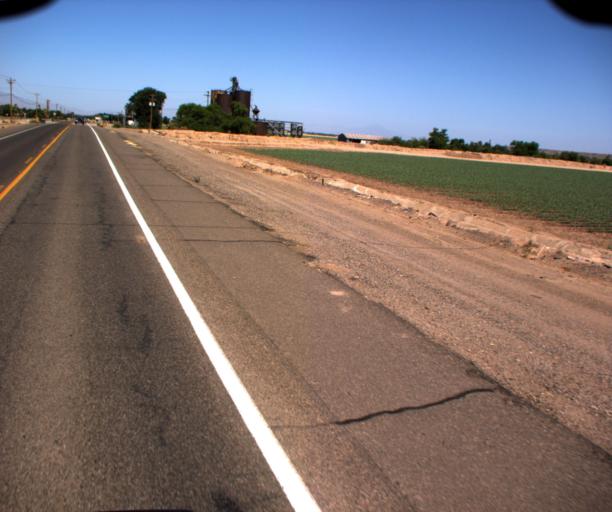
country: US
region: Arizona
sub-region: Graham County
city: Safford
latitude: 32.8166
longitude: -109.6462
